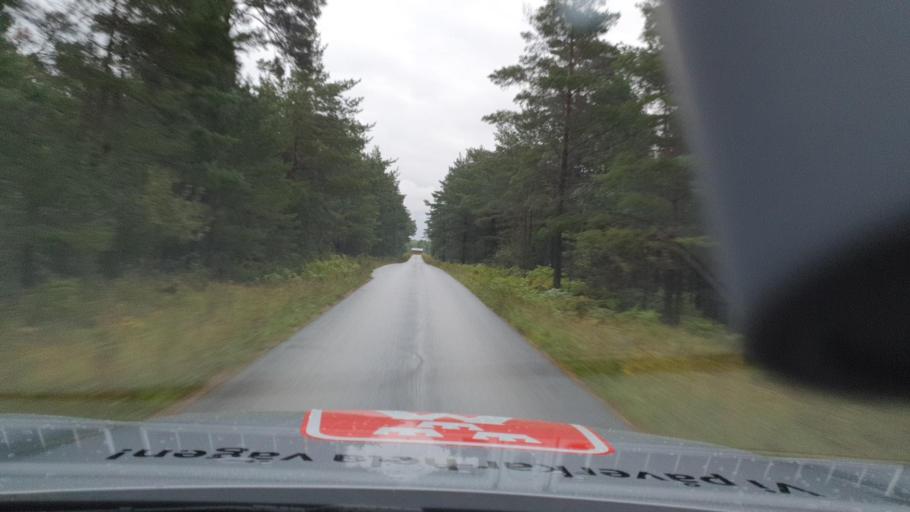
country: SE
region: Gotland
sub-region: Gotland
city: Slite
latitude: 57.8089
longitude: 18.5852
